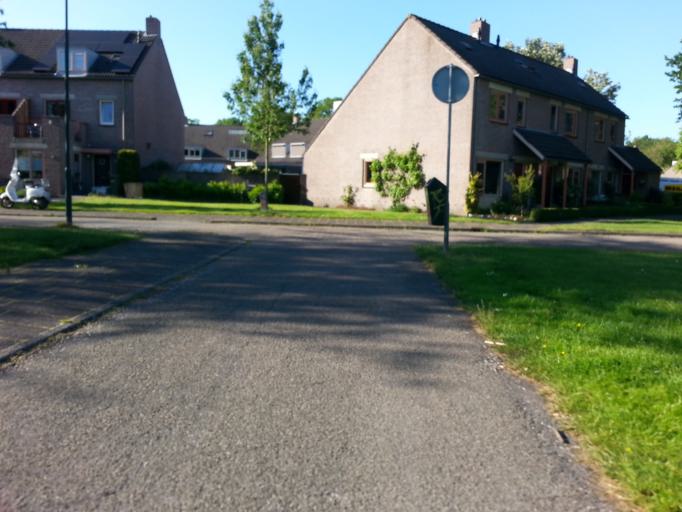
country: NL
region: Utrecht
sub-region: Gemeente Leusden
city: Leusden
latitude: 52.1294
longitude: 5.4363
